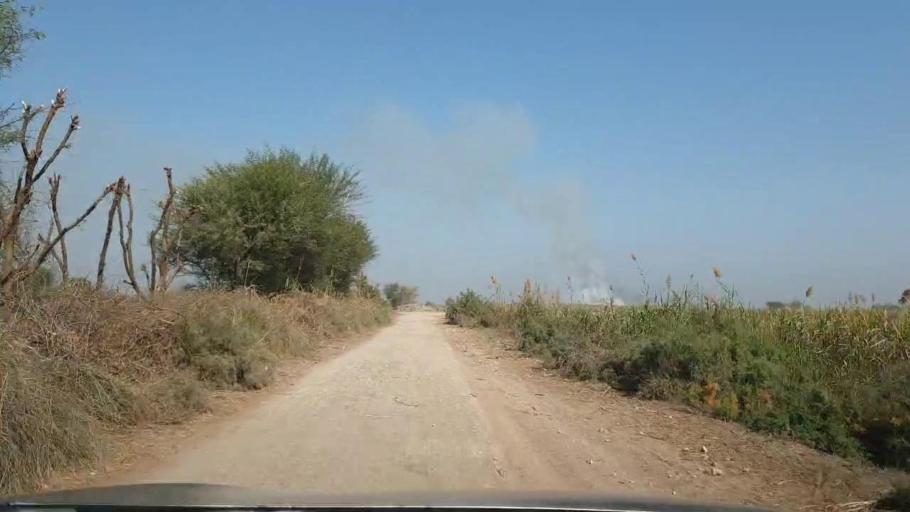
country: PK
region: Sindh
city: Berani
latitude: 25.6453
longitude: 68.8959
